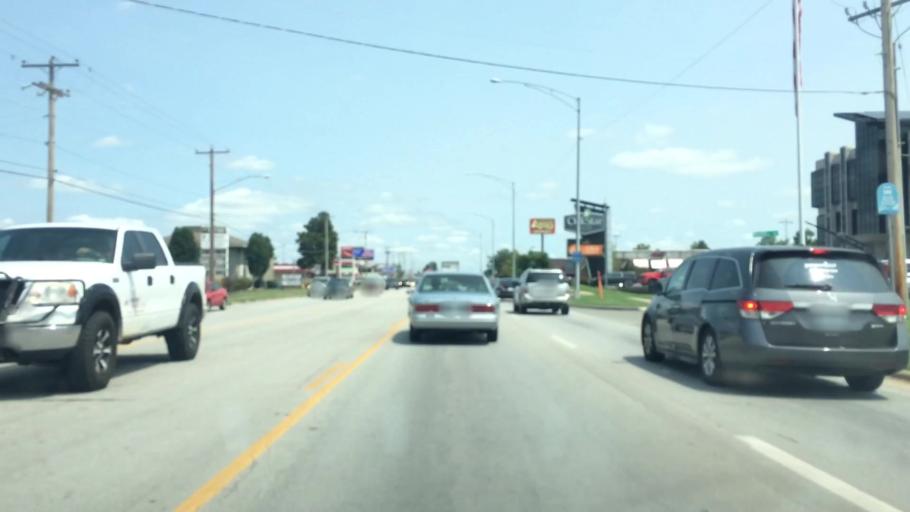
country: US
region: Missouri
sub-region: Greene County
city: Springfield
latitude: 37.1596
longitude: -93.2817
